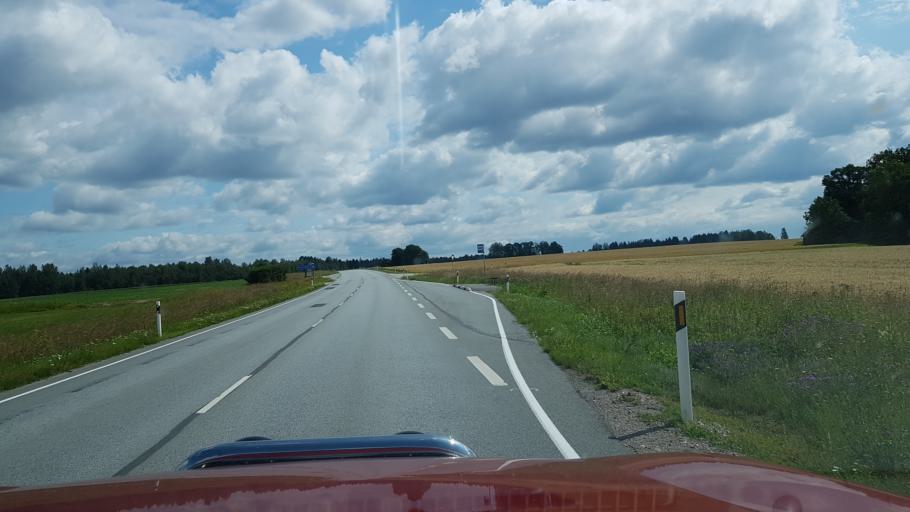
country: EE
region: Jogevamaa
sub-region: Jogeva linn
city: Jogeva
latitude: 58.8159
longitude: 26.5566
